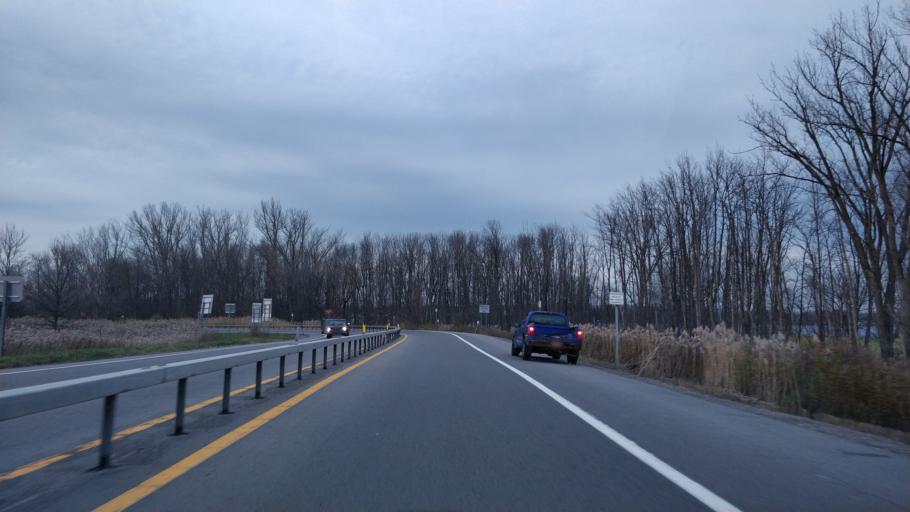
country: US
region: New York
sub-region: Onondaga County
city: Brewerton
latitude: 43.2315
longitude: -76.1268
